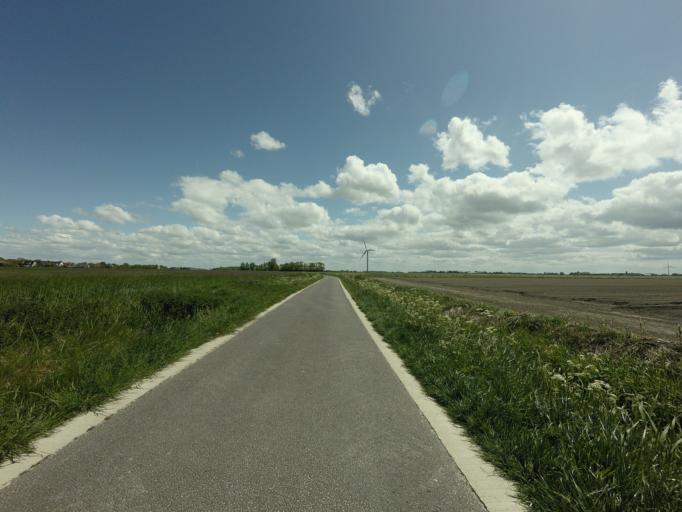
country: NL
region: Friesland
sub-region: Gemeente Harlingen
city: Harlingen
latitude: 53.1378
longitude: 5.4270
